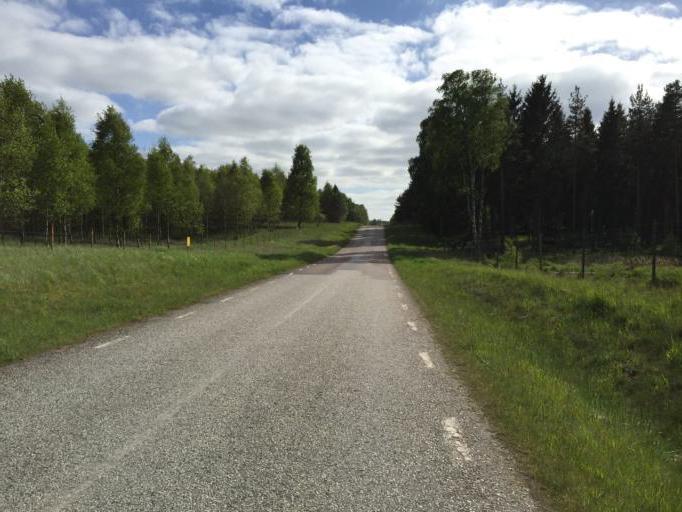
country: SE
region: Skane
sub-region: Sjobo Kommun
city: Blentarp
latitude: 55.6583
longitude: 13.6120
